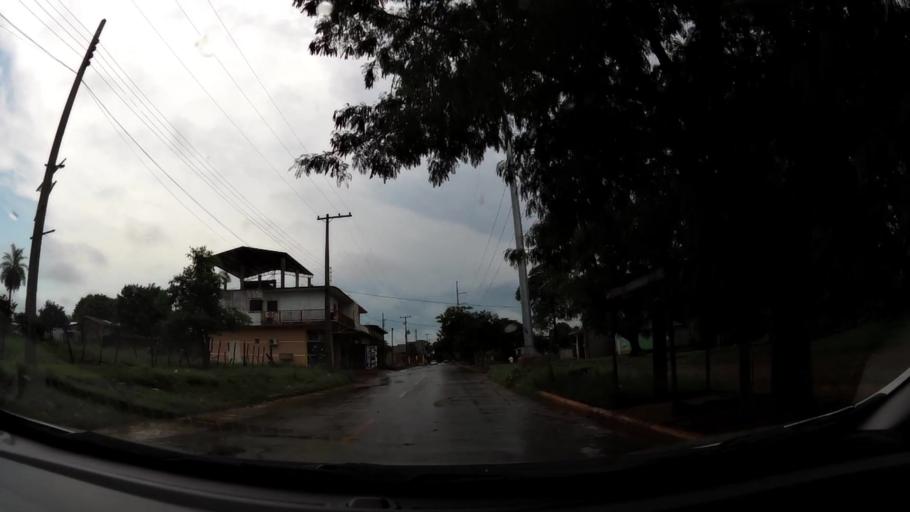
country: PY
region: Alto Parana
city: Presidente Franco
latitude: -25.5258
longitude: -54.6665
